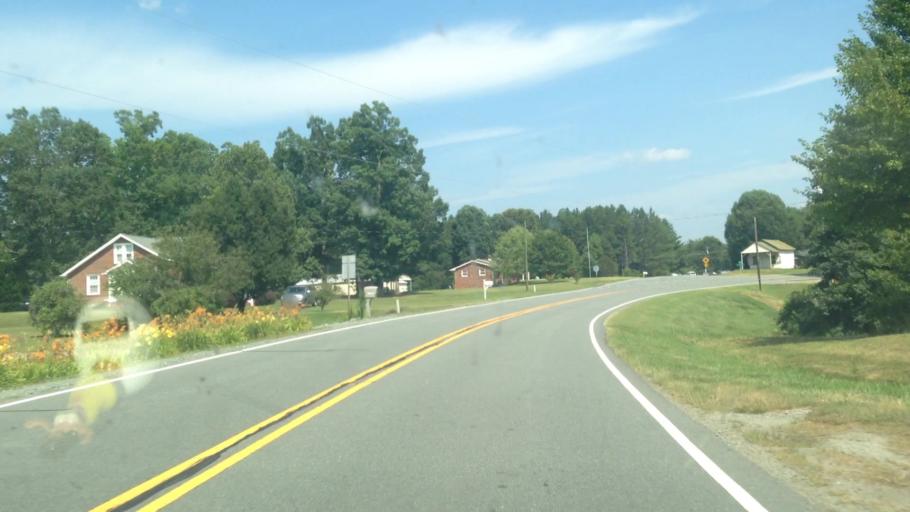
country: US
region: North Carolina
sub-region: Stokes County
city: Walnut Cove
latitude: 36.3717
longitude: -80.0711
